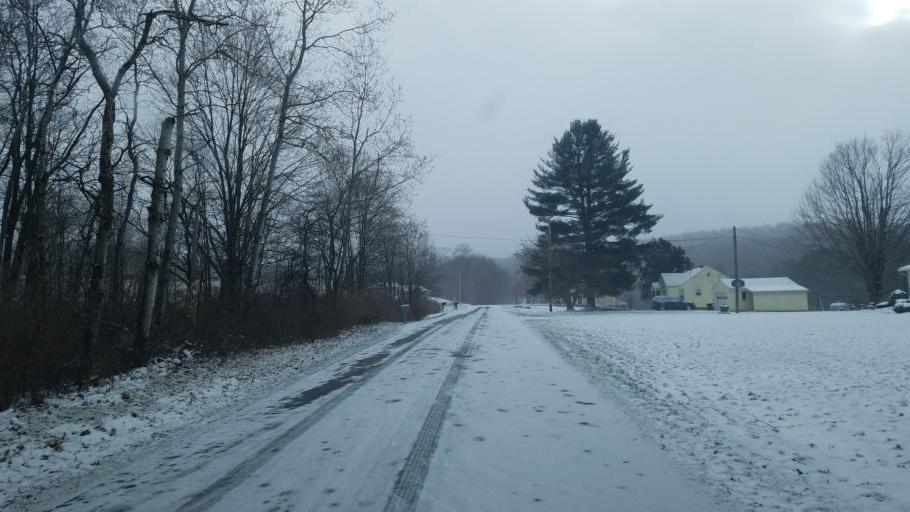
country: US
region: Pennsylvania
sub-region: Crawford County
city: Cochranton
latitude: 41.4713
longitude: -79.9654
